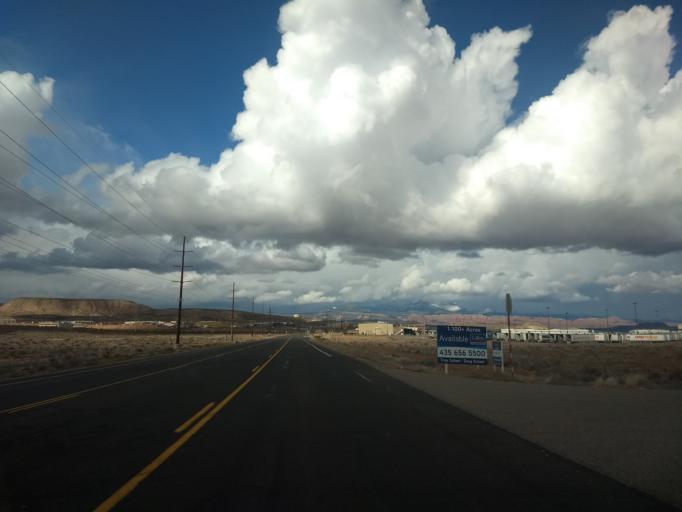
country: US
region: Utah
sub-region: Washington County
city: Saint George
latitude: 37.0231
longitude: -113.5630
